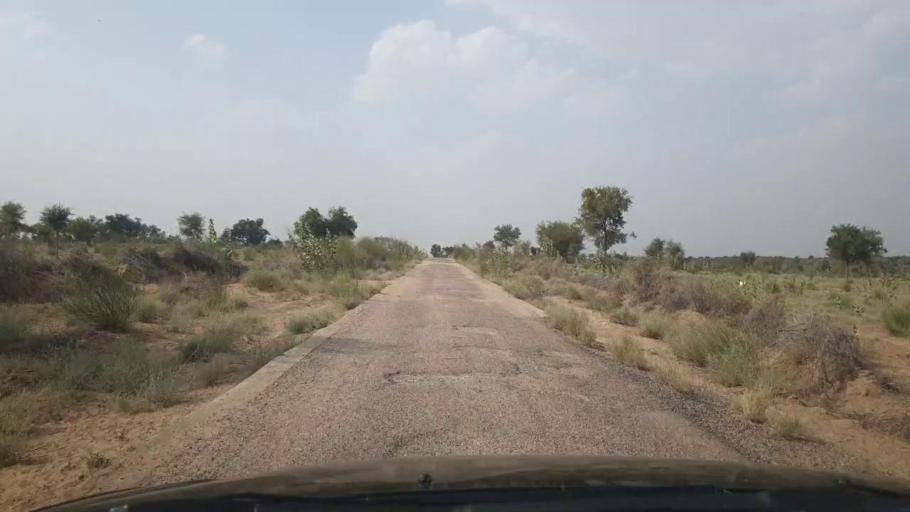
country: PK
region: Sindh
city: Islamkot
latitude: 24.9781
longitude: 70.5844
